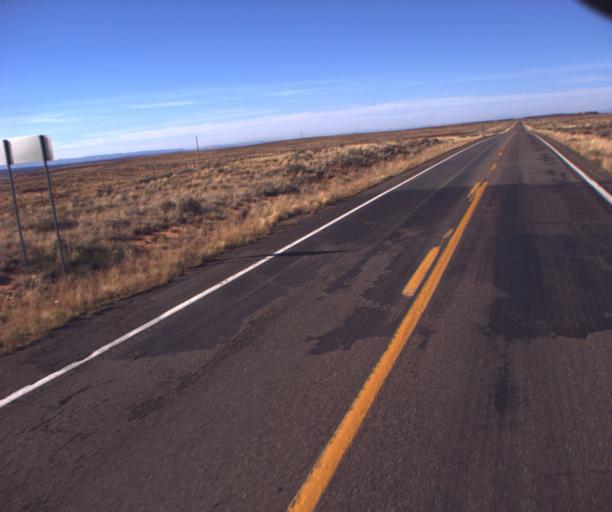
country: US
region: Arizona
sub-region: Coconino County
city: Kaibito
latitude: 36.7057
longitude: -111.2682
